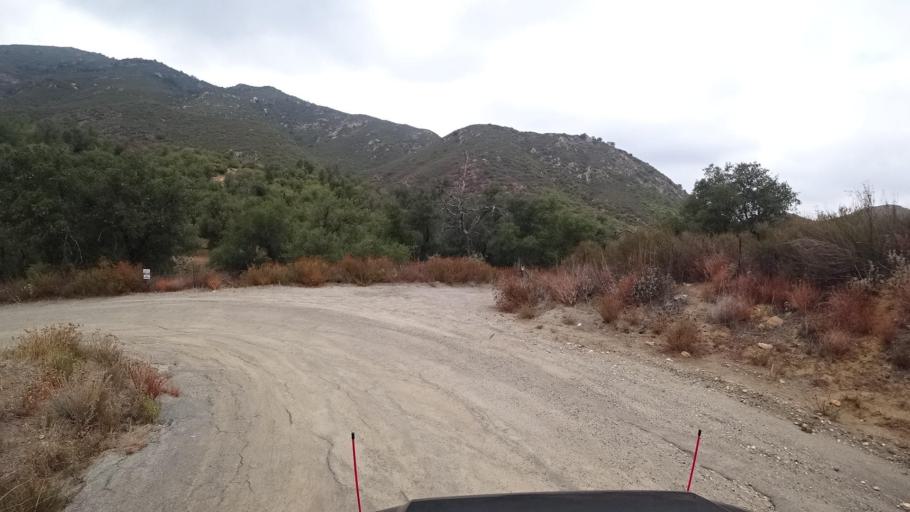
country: US
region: California
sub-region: San Diego County
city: San Diego Country Estates
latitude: 32.9695
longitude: -116.6737
